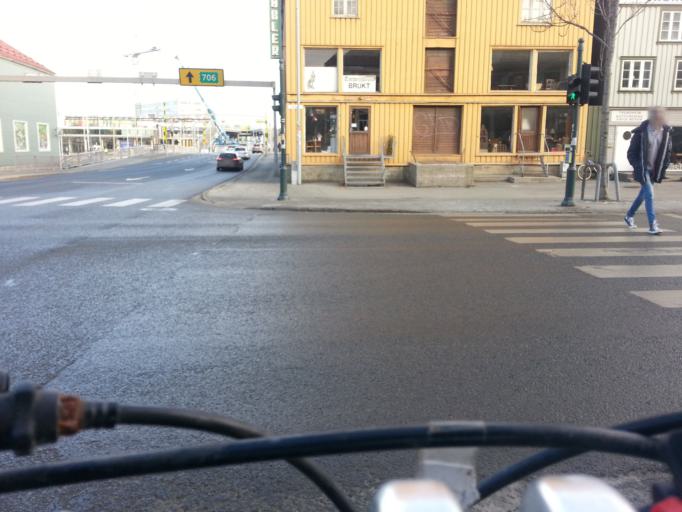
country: NO
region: Sor-Trondelag
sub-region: Trondheim
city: Trondheim
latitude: 63.4347
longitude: 10.4003
